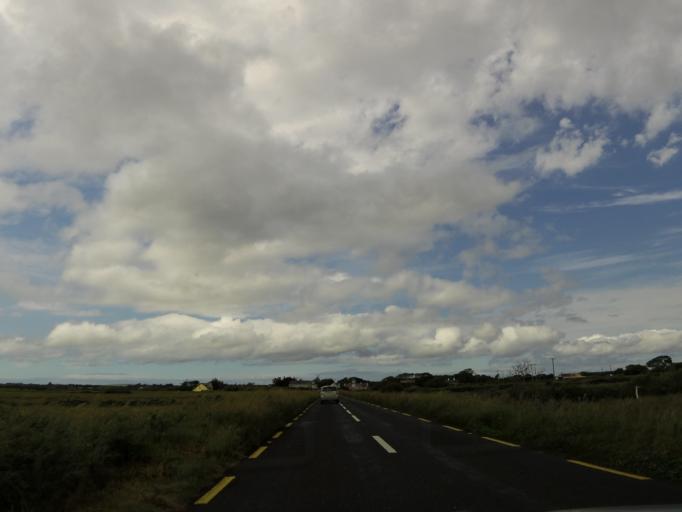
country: IE
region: Munster
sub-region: An Clar
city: Kilrush
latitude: 52.6648
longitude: -9.5348
